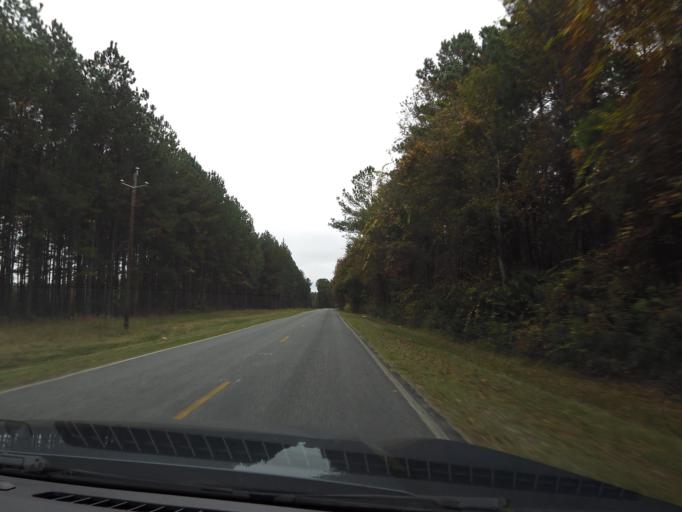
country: US
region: Georgia
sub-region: Charlton County
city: Folkston
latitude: 30.9142
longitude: -82.0833
